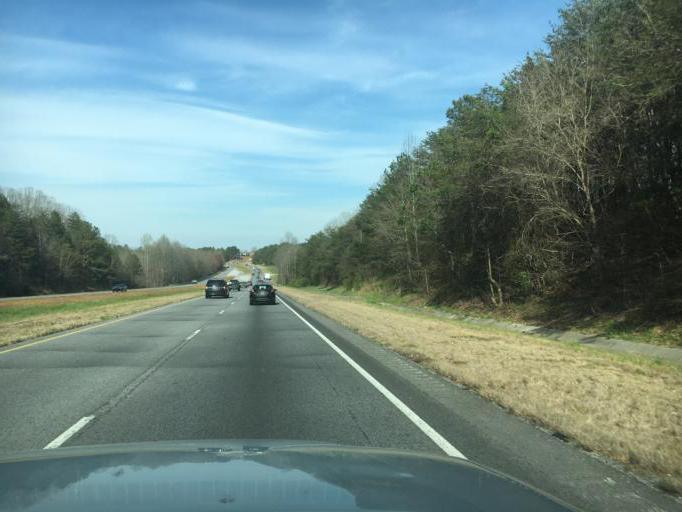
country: US
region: Georgia
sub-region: Hall County
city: Lula
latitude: 34.4119
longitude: -83.6634
